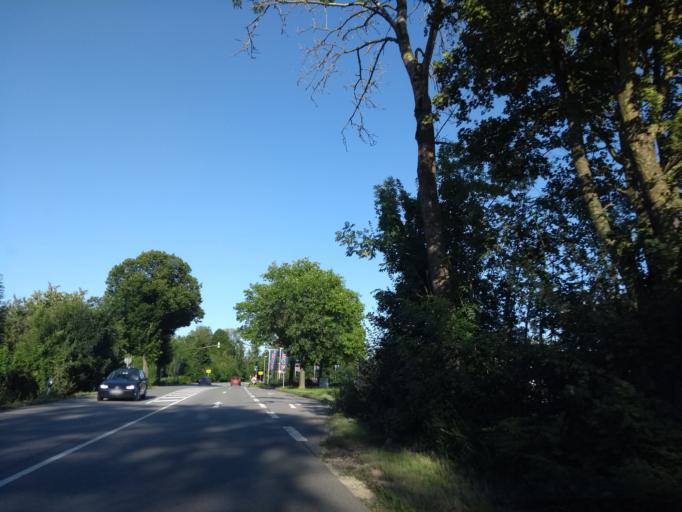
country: DE
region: Bavaria
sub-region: Upper Bavaria
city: Muehldorf
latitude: 48.2361
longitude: 12.5461
